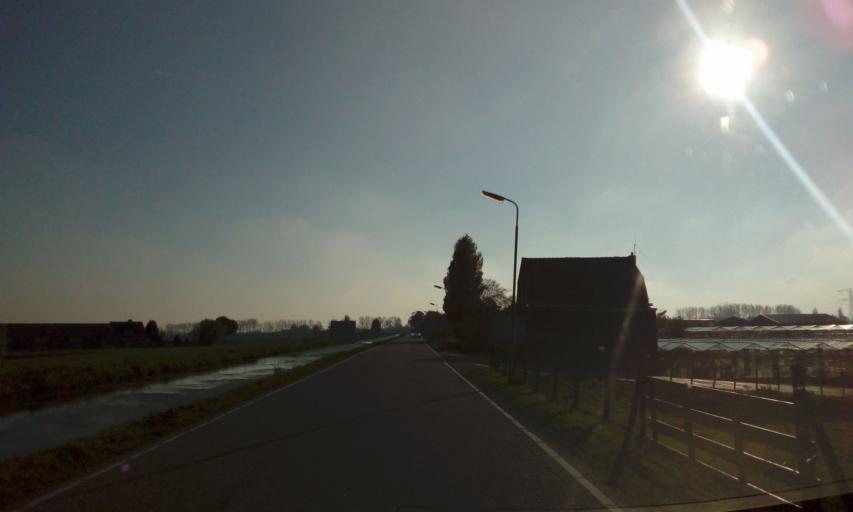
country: NL
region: South Holland
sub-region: Gemeente Lansingerland
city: Bleiswijk
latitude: 52.0353
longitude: 4.5777
